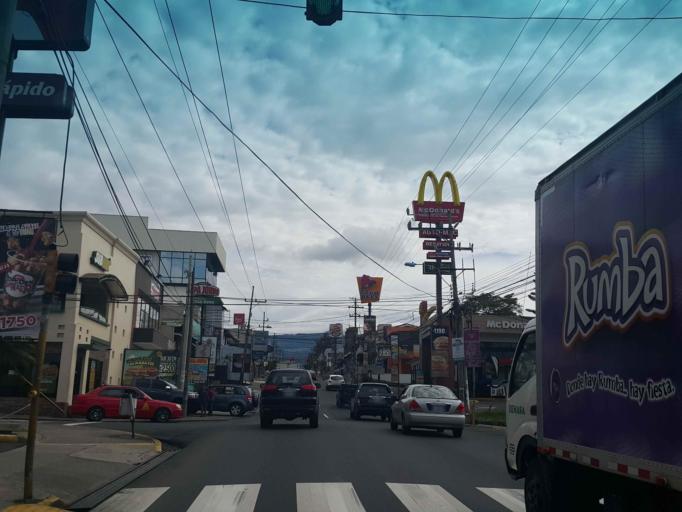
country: CR
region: Heredia
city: Heredia
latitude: 9.9957
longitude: -84.1125
